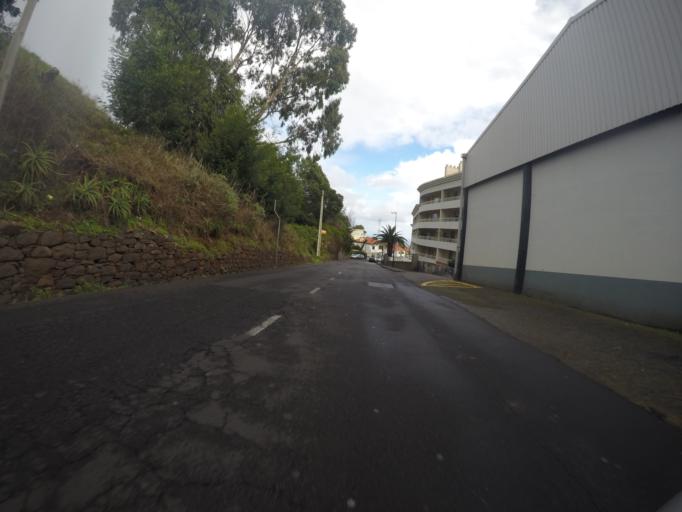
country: PT
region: Madeira
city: Canico
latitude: 32.6528
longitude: -16.8459
